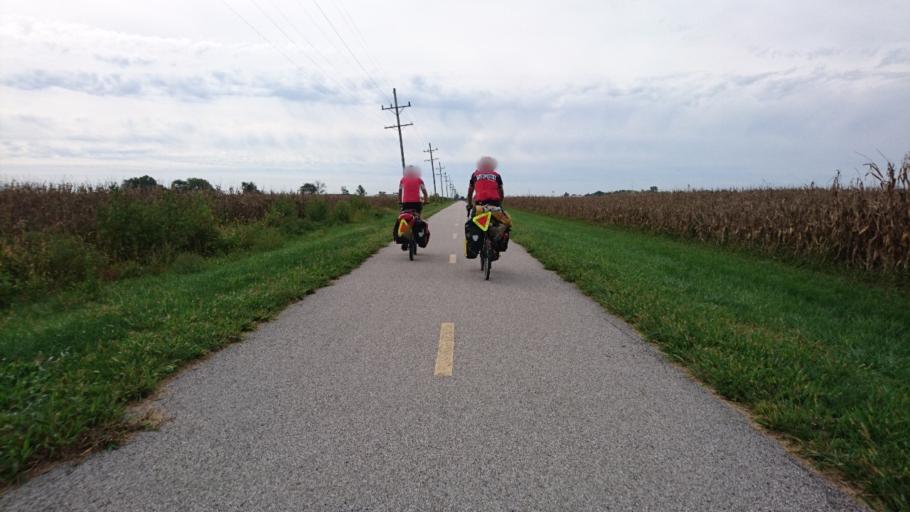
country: US
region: Illinois
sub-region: Madison County
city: Worden
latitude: 38.9031
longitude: -89.8379
